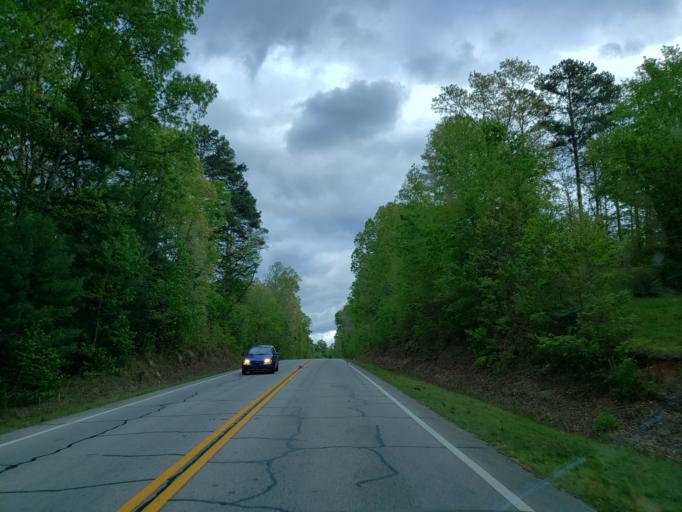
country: US
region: Georgia
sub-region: Haralson County
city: Buchanan
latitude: 33.8147
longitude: -85.1287
